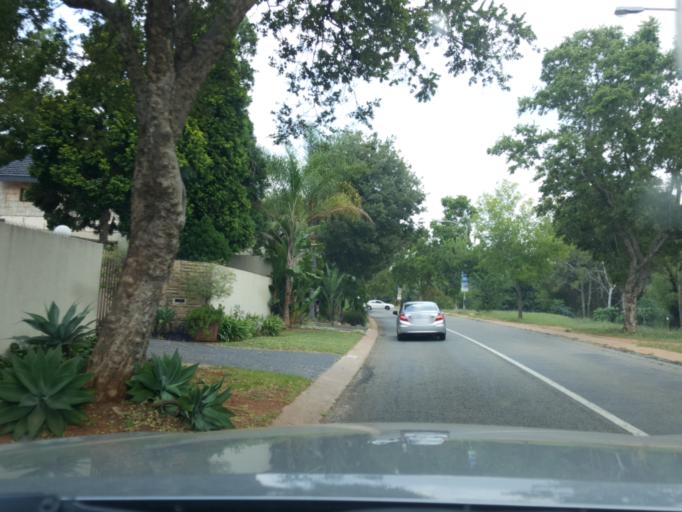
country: ZA
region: Gauteng
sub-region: City of Tshwane Metropolitan Municipality
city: Centurion
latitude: -25.8441
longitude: 28.2667
